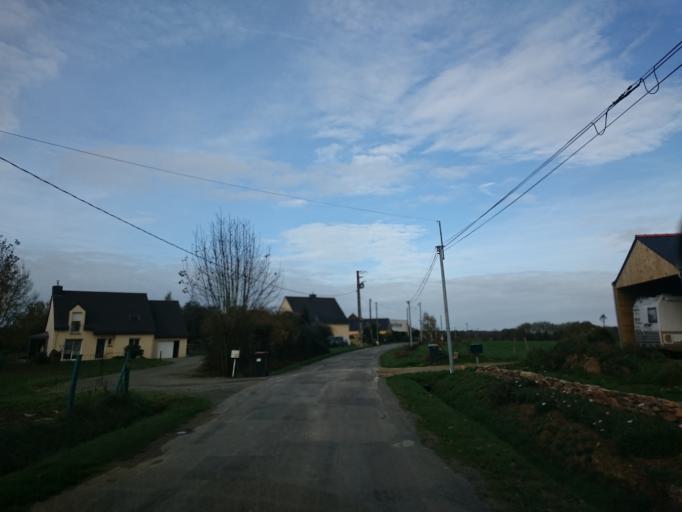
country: FR
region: Brittany
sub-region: Departement d'Ille-et-Vilaine
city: Chanteloup
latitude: 47.9422
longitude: -1.6322
